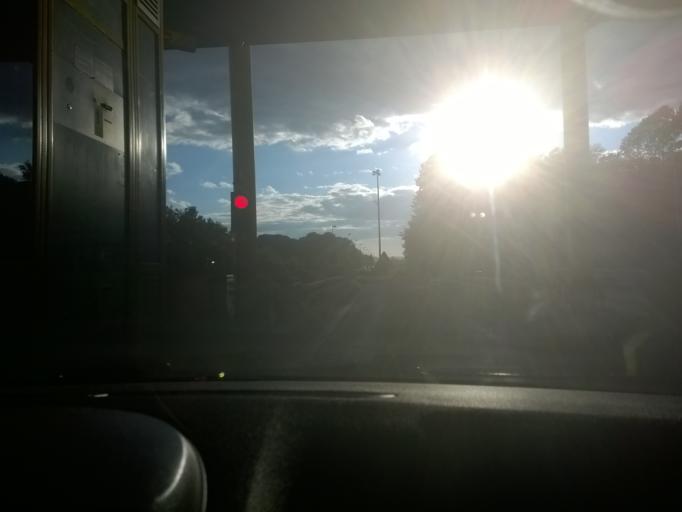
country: HR
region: Krapinsko-Zagorska
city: Oroslavje
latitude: 46.0034
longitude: 15.8766
